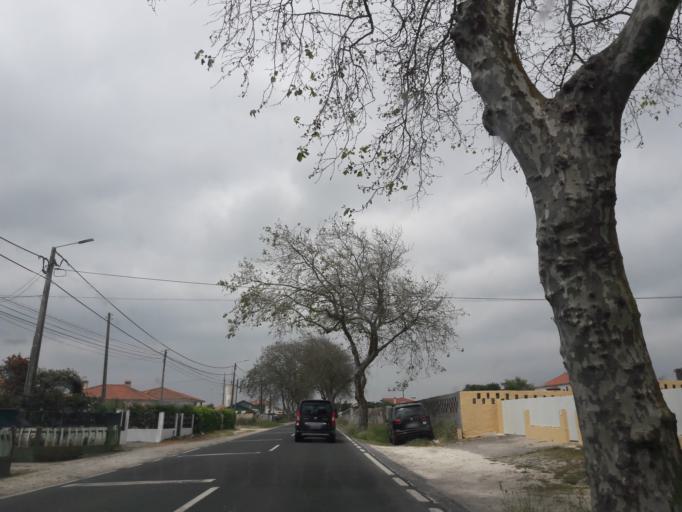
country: PT
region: Leiria
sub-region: Peniche
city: Atouguia da Baleia
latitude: 39.3329
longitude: -9.2623
